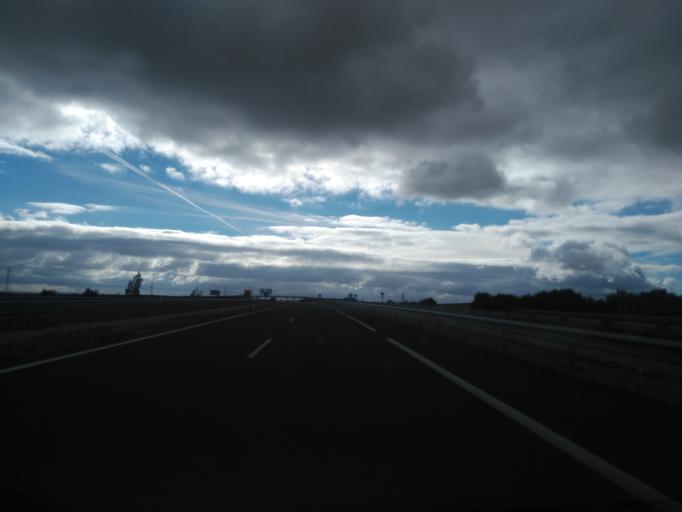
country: ES
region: Castille and Leon
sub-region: Provincia de Palencia
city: Abia de las Torres
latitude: 42.3999
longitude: -4.3884
